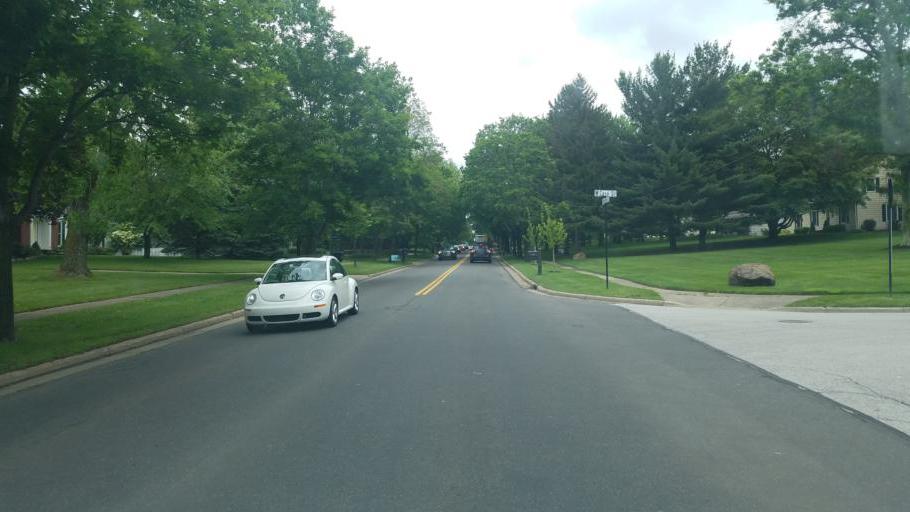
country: US
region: Ohio
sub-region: Summit County
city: Hudson
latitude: 41.2382
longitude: -81.4563
